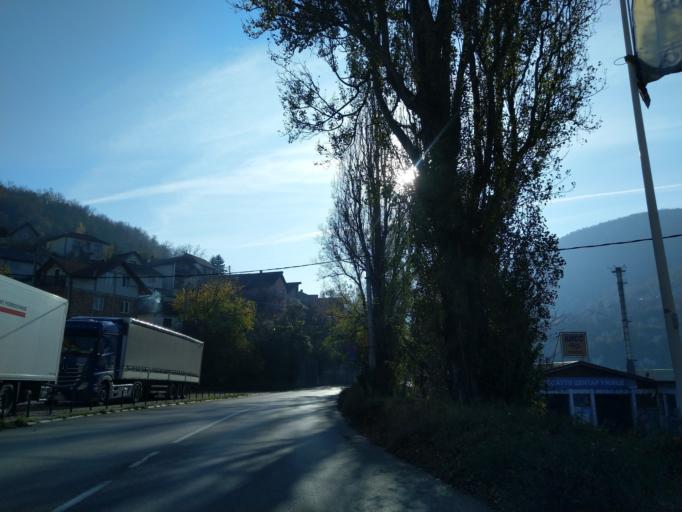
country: RS
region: Central Serbia
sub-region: Zlatiborski Okrug
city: Uzice
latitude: 43.8457
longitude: 19.8632
